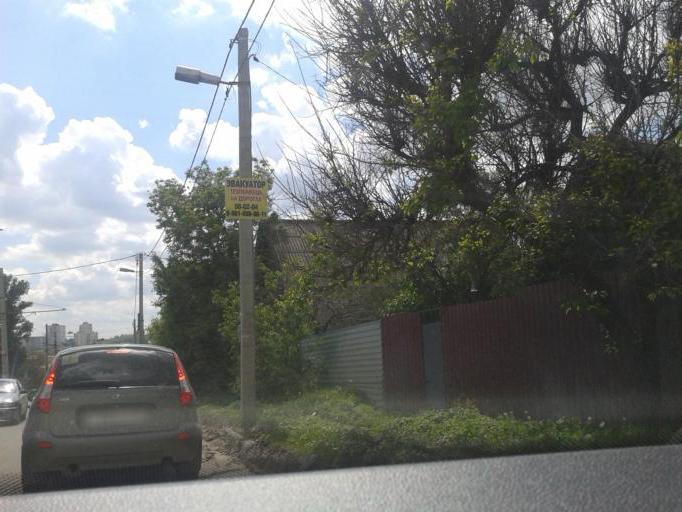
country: RU
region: Volgograd
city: Volgograd
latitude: 48.6916
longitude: 44.4543
